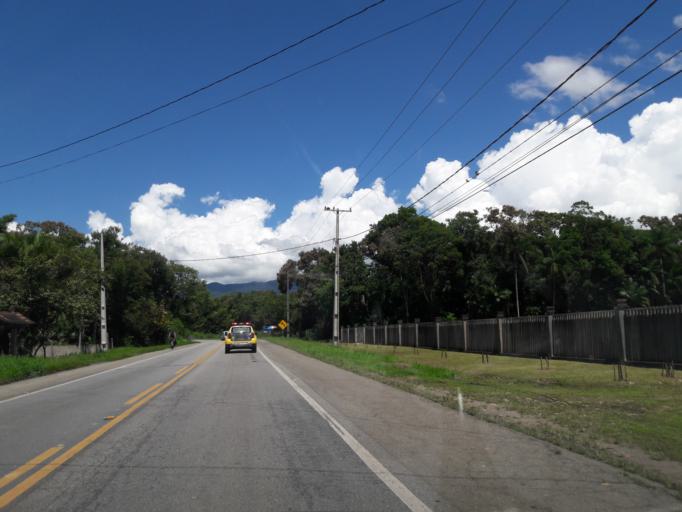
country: BR
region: Parana
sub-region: Antonina
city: Antonina
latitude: -25.5071
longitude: -48.8136
